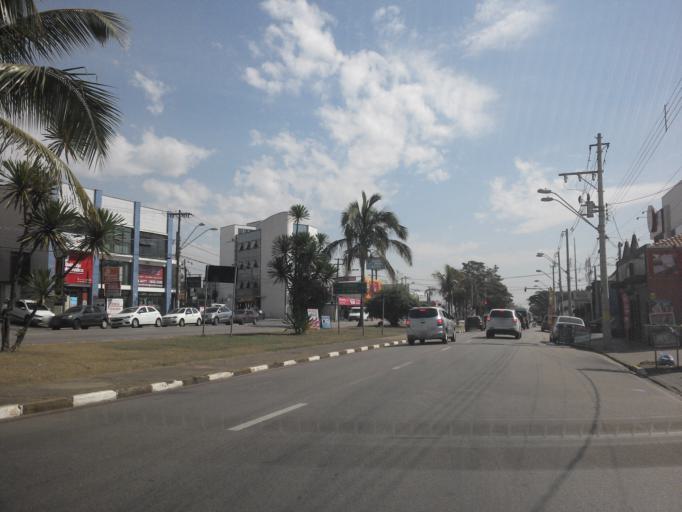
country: BR
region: Sao Paulo
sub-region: Sumare
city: Sumare
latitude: -22.8240
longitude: -47.2706
